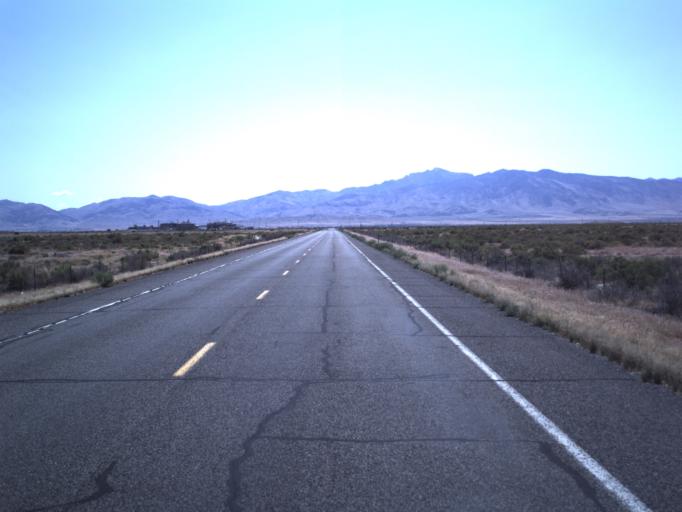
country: US
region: Utah
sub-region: Millard County
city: Delta
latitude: 39.4698
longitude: -112.4585
